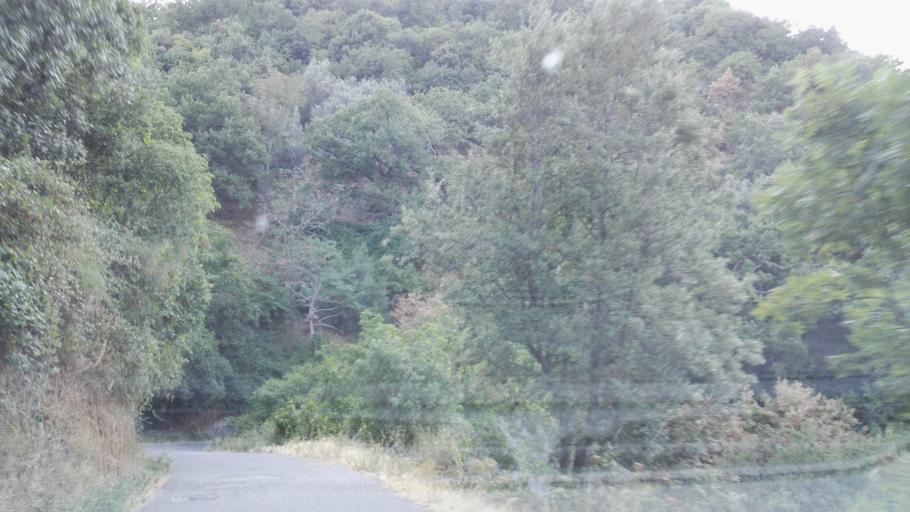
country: IT
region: Calabria
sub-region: Provincia di Reggio Calabria
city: Caulonia
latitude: 38.4134
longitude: 16.3704
